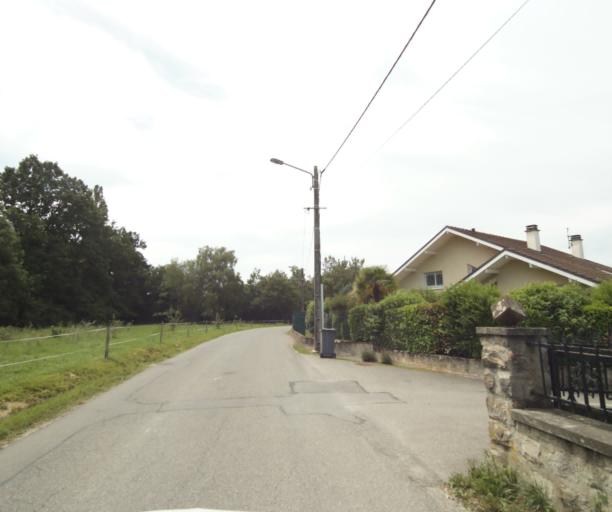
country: FR
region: Rhone-Alpes
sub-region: Departement de la Haute-Savoie
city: Anthy-sur-Leman
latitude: 46.3514
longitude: 6.4133
